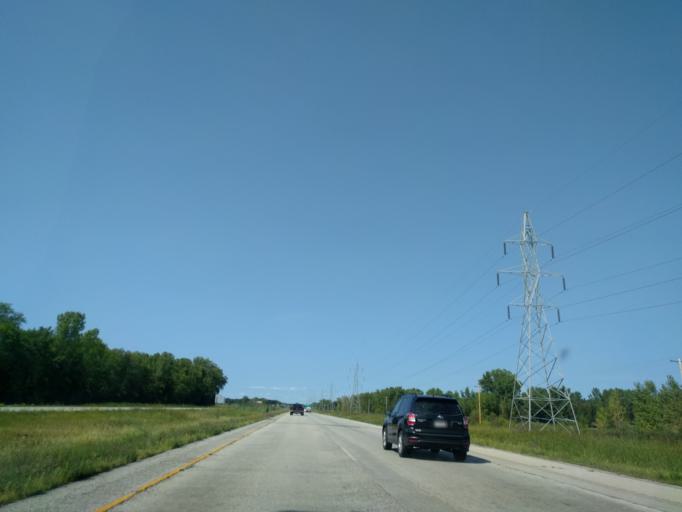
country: US
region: Wisconsin
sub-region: Brown County
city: Suamico
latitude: 44.6093
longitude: -88.0500
